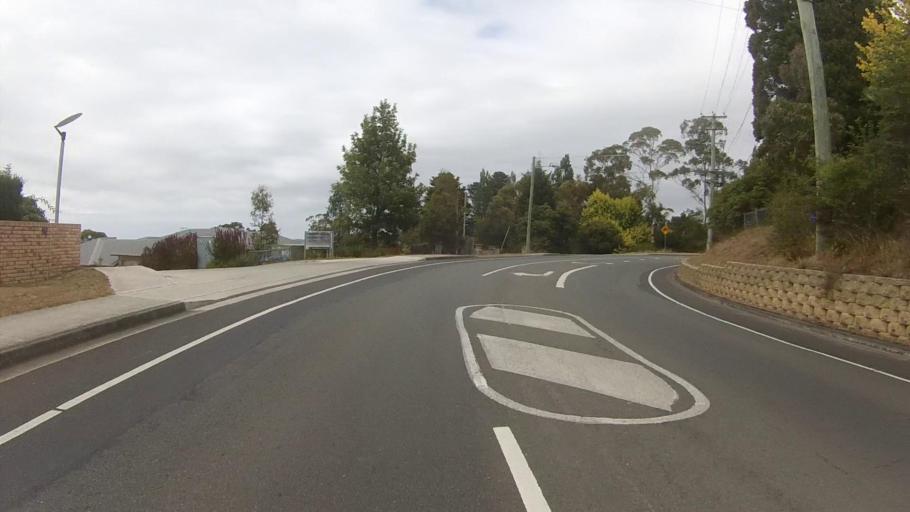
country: AU
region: Tasmania
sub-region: Kingborough
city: Taroona
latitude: -42.9335
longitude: 147.3556
